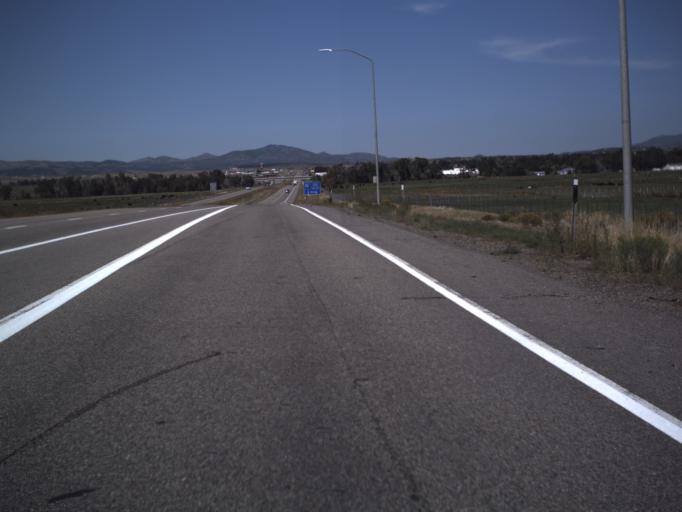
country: US
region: Utah
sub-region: Beaver County
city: Beaver
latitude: 38.2530
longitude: -112.6498
